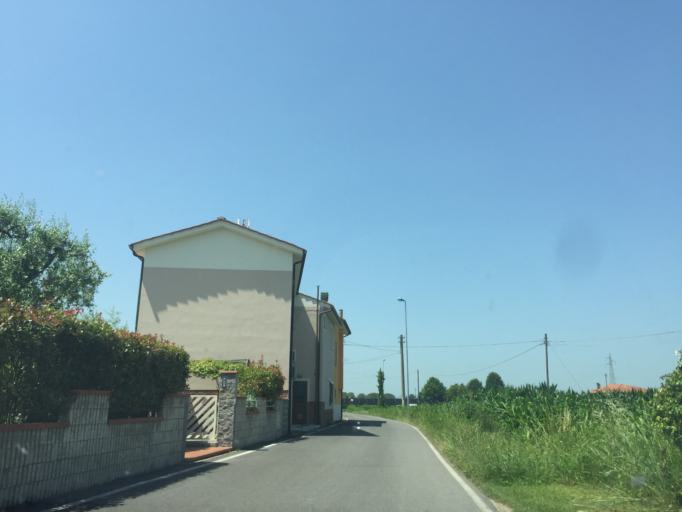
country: IT
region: Tuscany
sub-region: Provincia di Pistoia
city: Anchione
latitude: 43.8344
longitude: 10.7541
